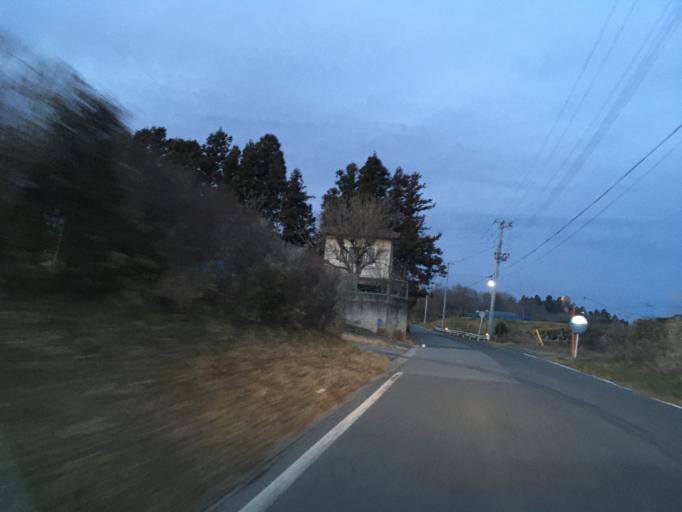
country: JP
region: Miyagi
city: Kogota
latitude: 38.6912
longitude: 141.0954
